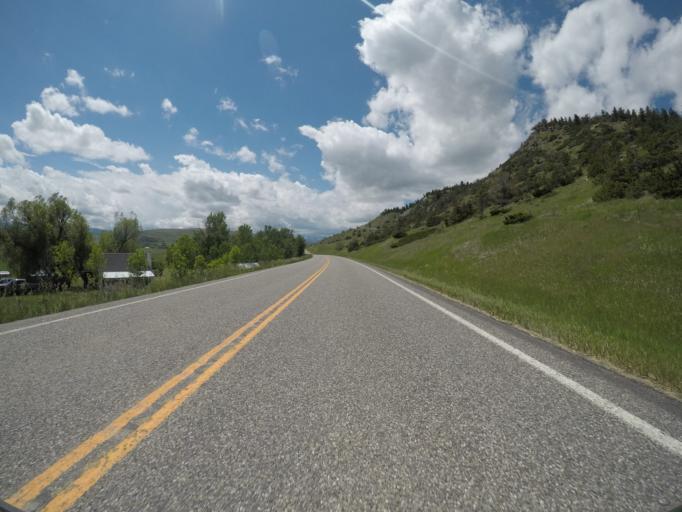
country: US
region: Montana
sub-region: Sweet Grass County
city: Big Timber
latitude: 45.6698
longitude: -110.1025
